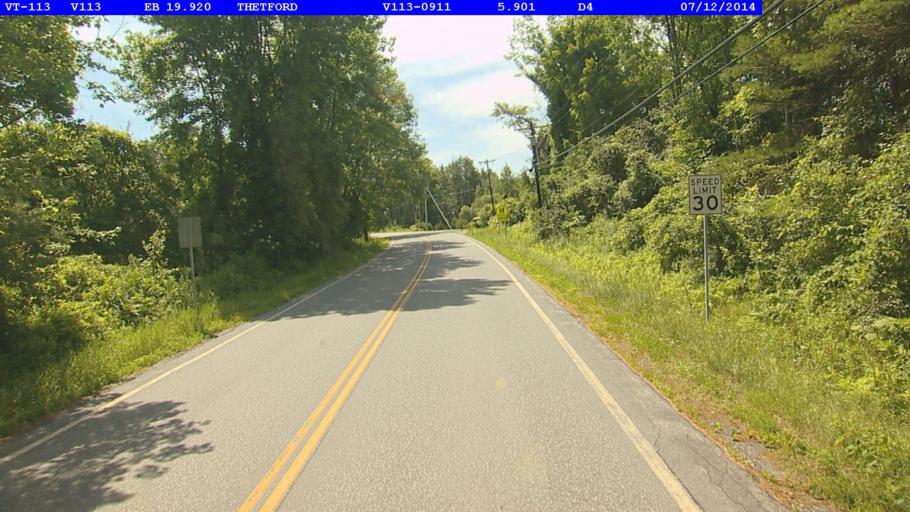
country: US
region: New Hampshire
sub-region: Grafton County
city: Lyme
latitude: 43.8220
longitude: -72.2340
